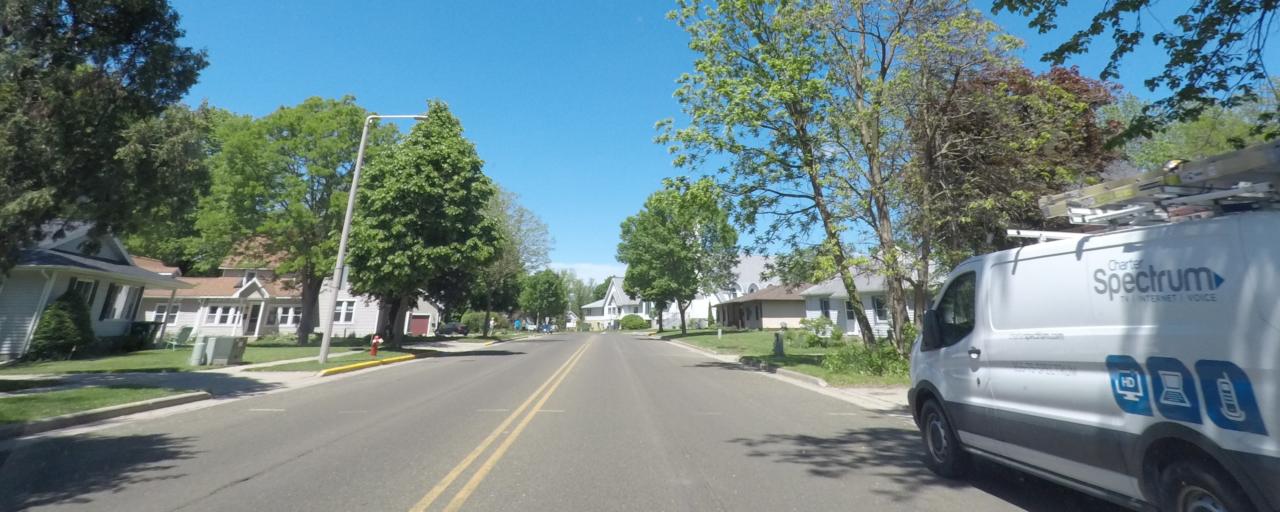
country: US
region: Wisconsin
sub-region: Dane County
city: Verona
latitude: 42.9826
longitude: -89.5340
